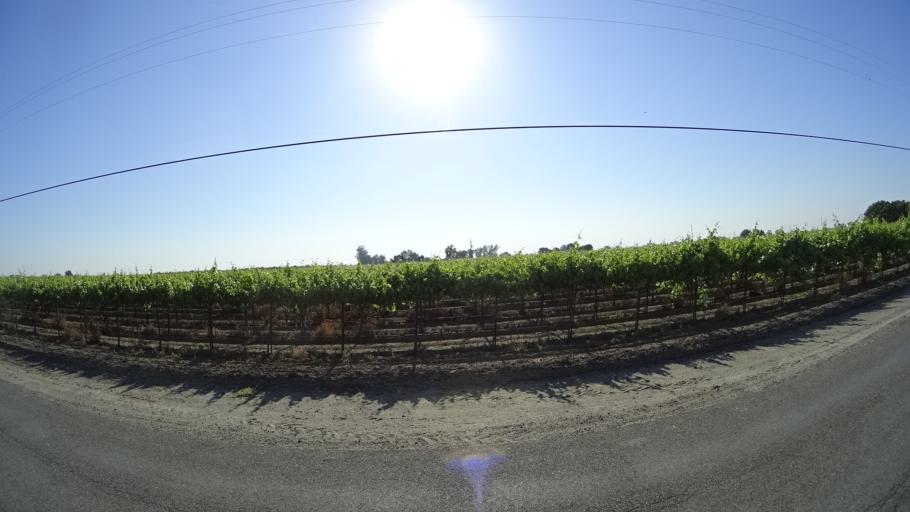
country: US
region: California
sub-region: Fresno County
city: Riverdale
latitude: 36.3682
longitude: -119.8693
